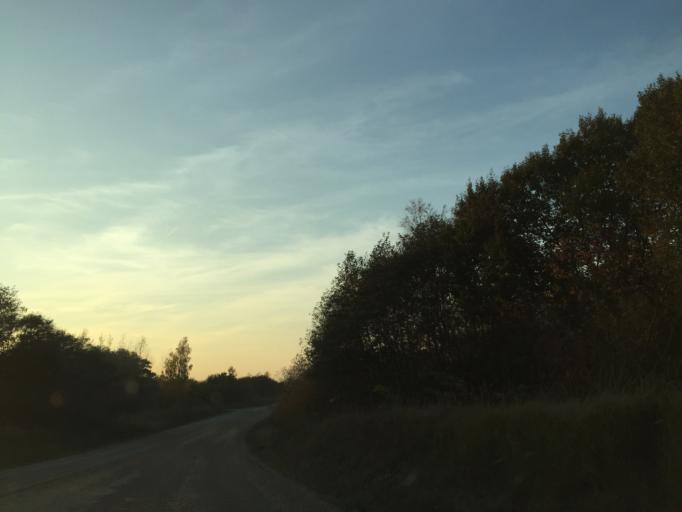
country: LV
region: Priekule
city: Priekule
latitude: 56.4713
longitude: 21.5945
